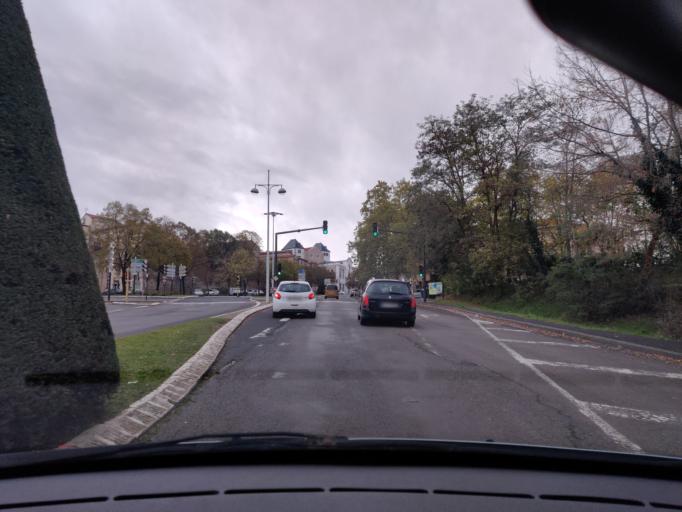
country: FR
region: Auvergne
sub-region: Departement du Puy-de-Dome
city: Riom
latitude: 45.8962
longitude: 3.1124
